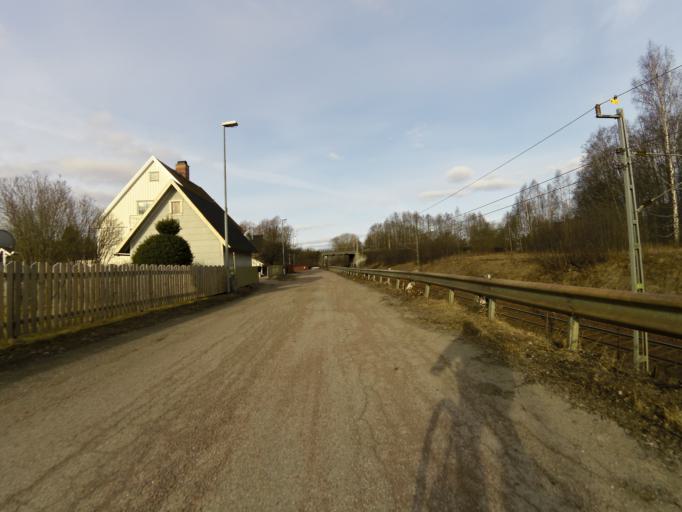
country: SE
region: Gaevleborg
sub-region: Gavle Kommun
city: Gavle
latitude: 60.6826
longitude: 17.1249
